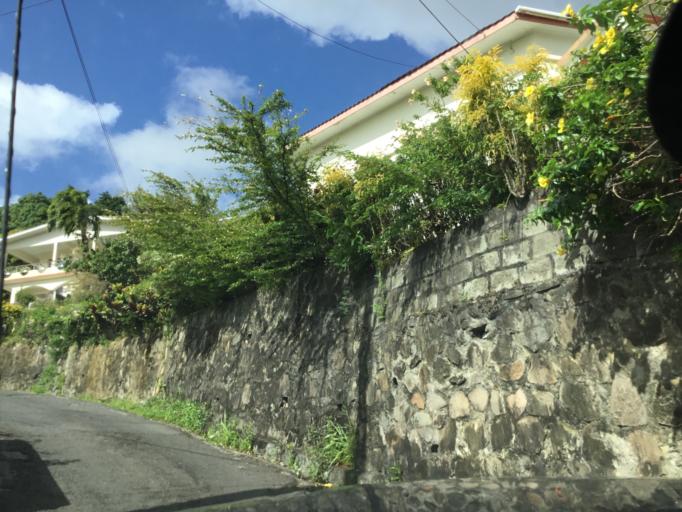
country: VC
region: Saint George
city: Kingstown
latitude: 13.1624
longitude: -61.2169
